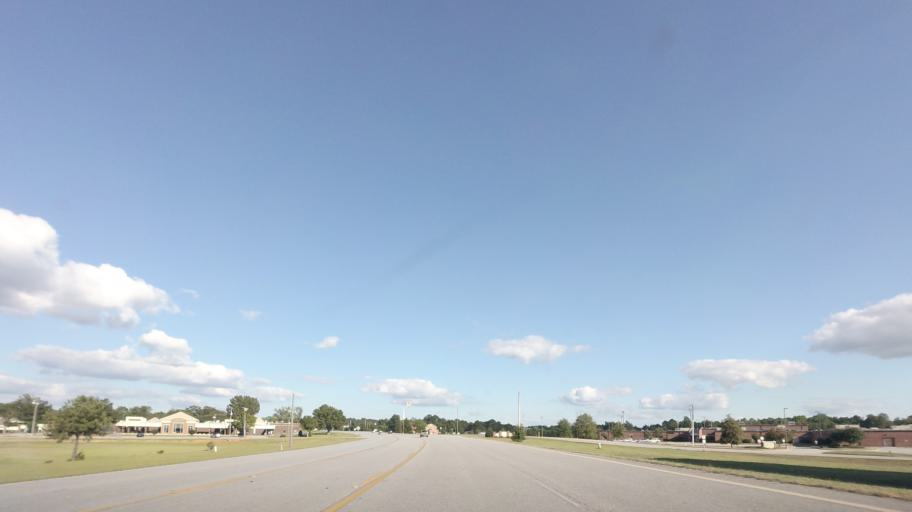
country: US
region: Georgia
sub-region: Lamar County
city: Barnesville
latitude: 33.0471
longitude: -84.1785
